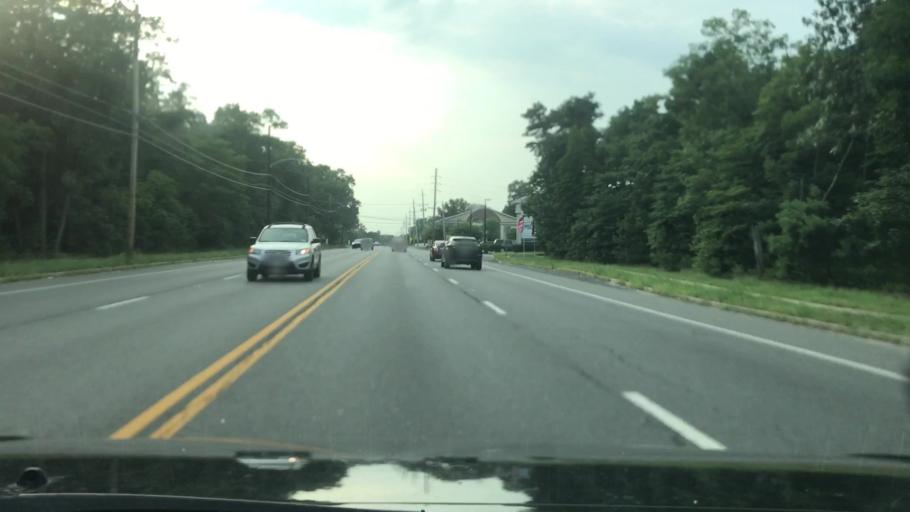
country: US
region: New Jersey
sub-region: Ocean County
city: Lakewood
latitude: 40.0837
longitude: -74.2040
